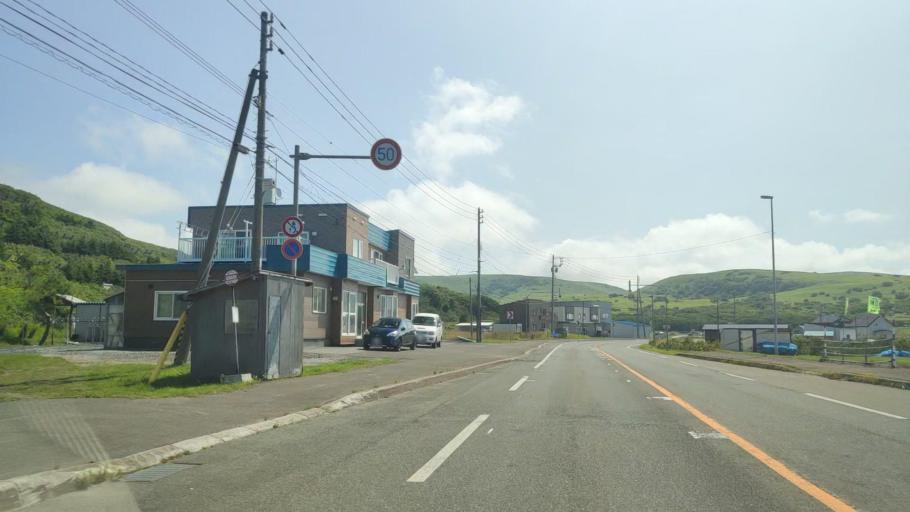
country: JP
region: Hokkaido
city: Makubetsu
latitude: 45.4636
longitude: 141.8785
